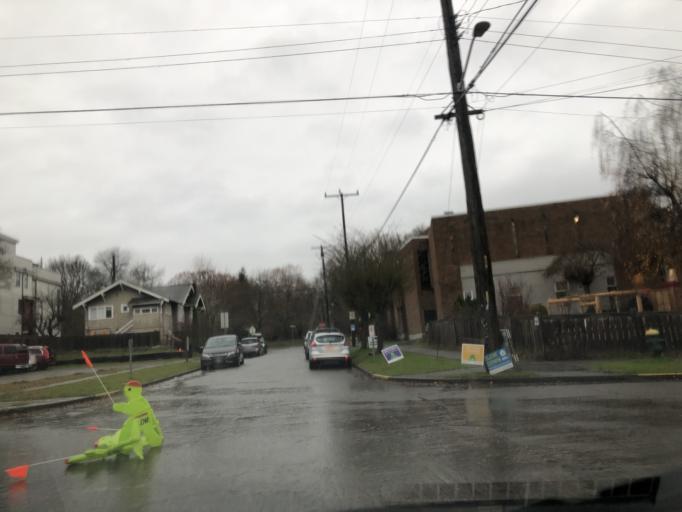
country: US
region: Washington
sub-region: King County
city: Seattle
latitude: 47.6642
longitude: -122.3527
